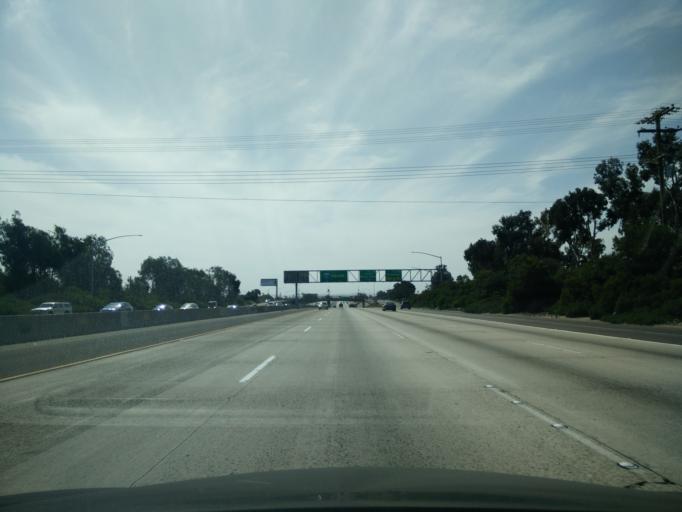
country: US
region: California
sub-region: San Diego County
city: Chula Vista
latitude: 32.6329
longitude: -117.0975
